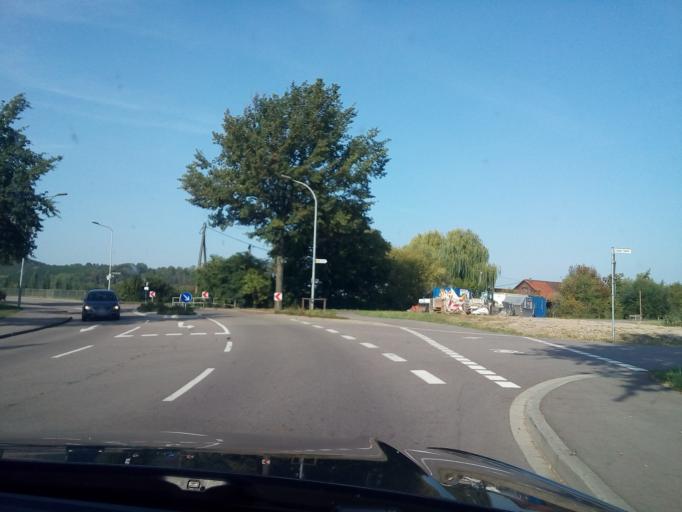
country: DE
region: Baden-Wuerttemberg
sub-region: Freiburg Region
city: Oberkirch
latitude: 48.5376
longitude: 8.0594
